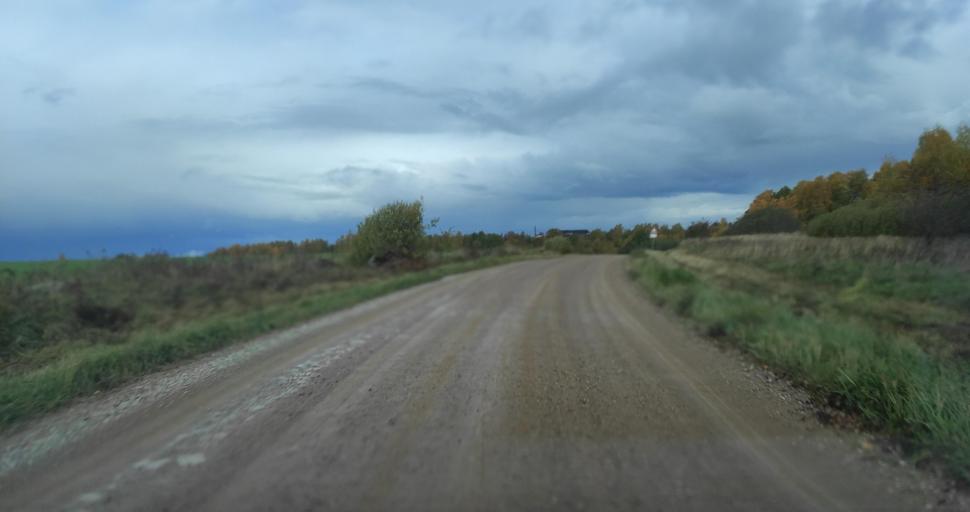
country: LV
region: Vainode
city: Vainode
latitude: 56.5587
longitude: 21.9070
